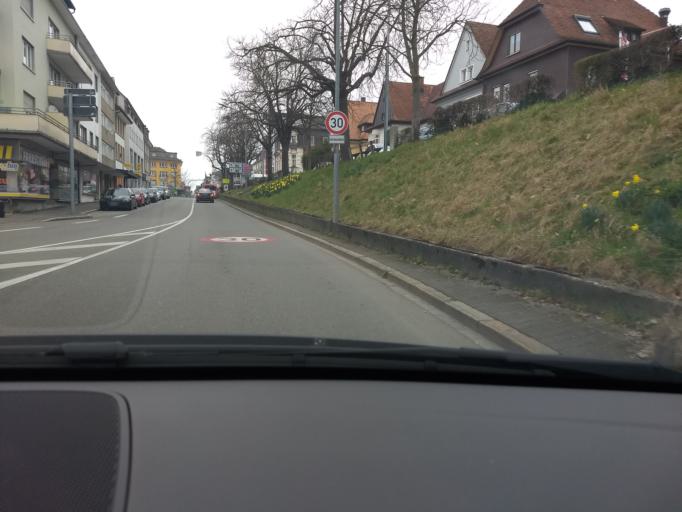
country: DE
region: Baden-Wuerttemberg
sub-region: Freiburg Region
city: Rheinfelden (Baden)
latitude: 47.5580
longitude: 7.7870
